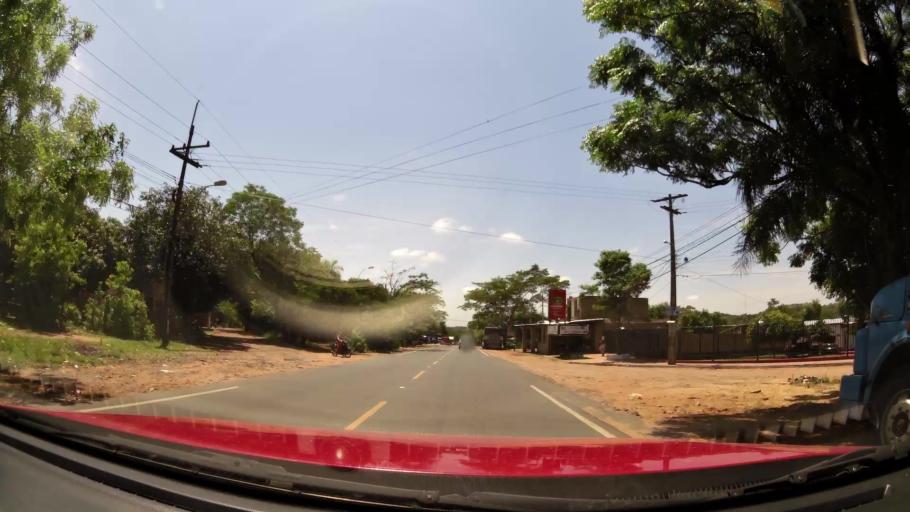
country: PY
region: Central
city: San Antonio
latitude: -25.4074
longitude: -57.5450
